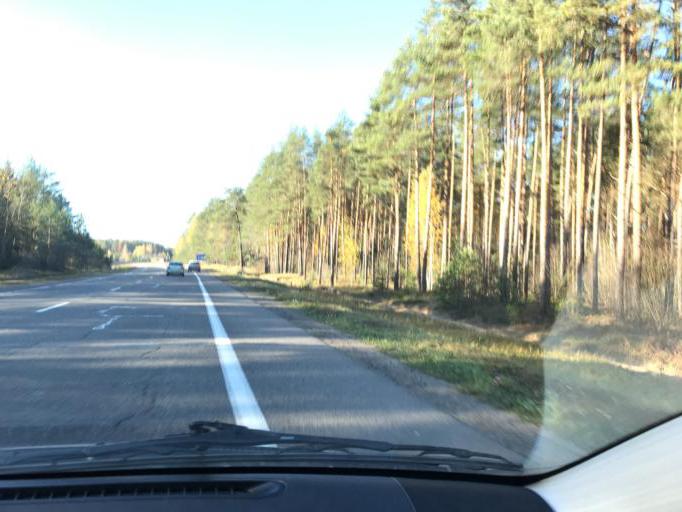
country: BY
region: Vitebsk
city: Syanno
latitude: 55.0664
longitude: 29.5344
